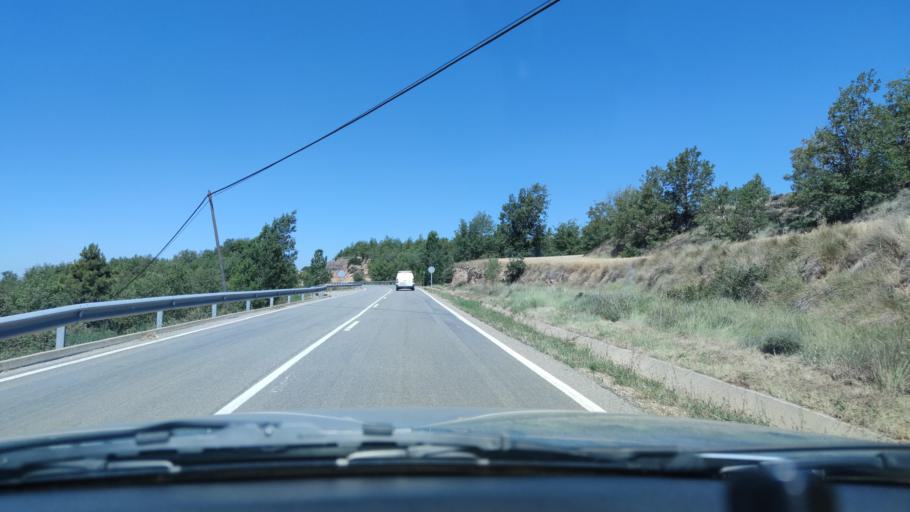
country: ES
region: Catalonia
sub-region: Provincia de Lleida
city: Solsona
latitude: 41.9122
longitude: 1.5165
